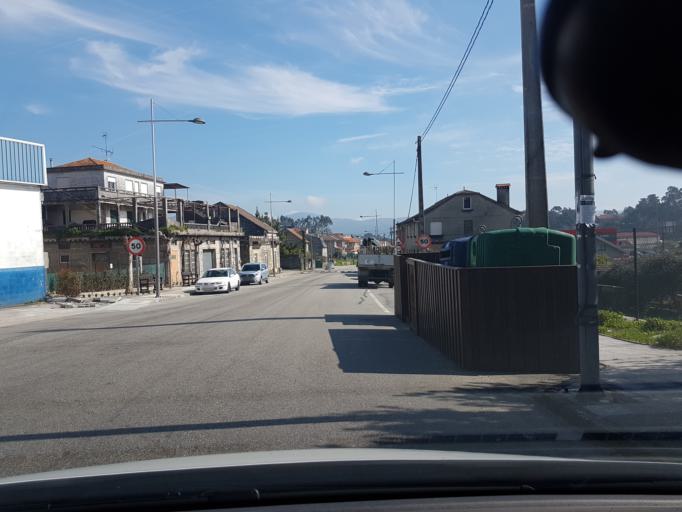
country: ES
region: Galicia
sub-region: Provincia de Pontevedra
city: Porrino
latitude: 42.1949
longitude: -8.6511
